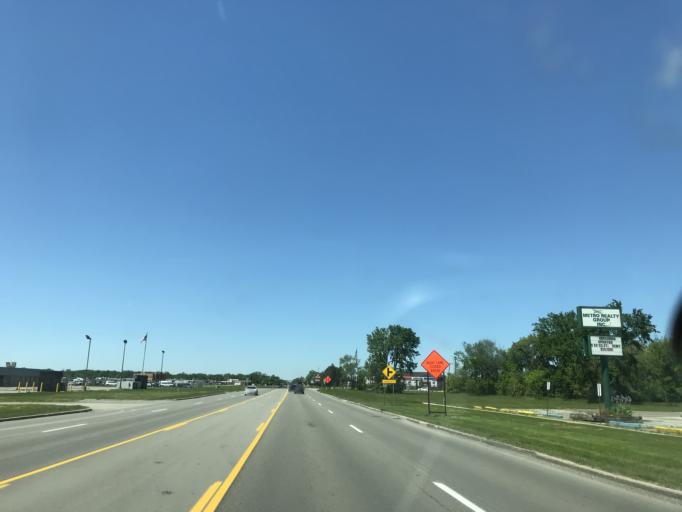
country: US
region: Michigan
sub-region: Wayne County
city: Taylor
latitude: 42.2297
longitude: -83.3274
